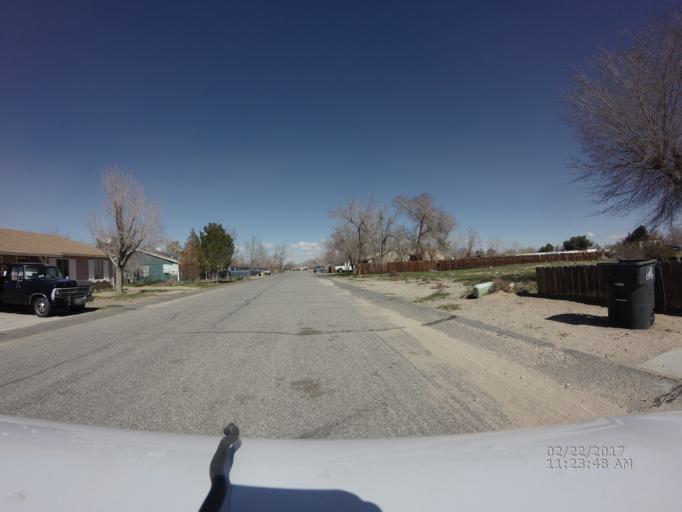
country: US
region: California
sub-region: Los Angeles County
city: Lake Los Angeles
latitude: 34.6204
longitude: -117.8128
